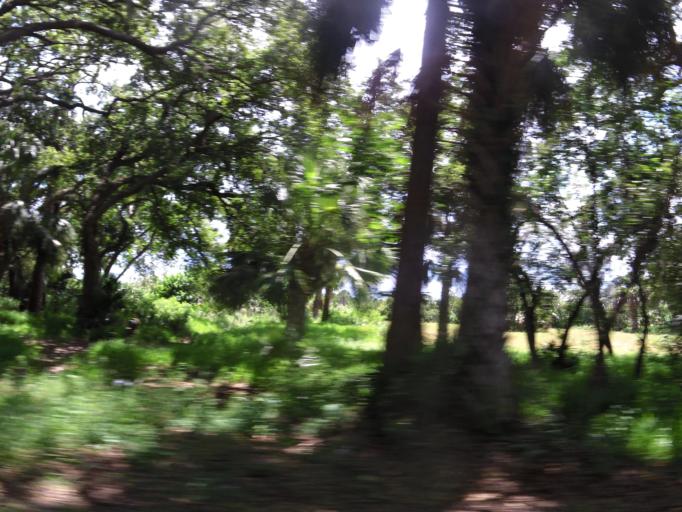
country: US
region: Florida
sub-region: Volusia County
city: Ormond-by-the-Sea
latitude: 29.3480
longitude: -81.0959
